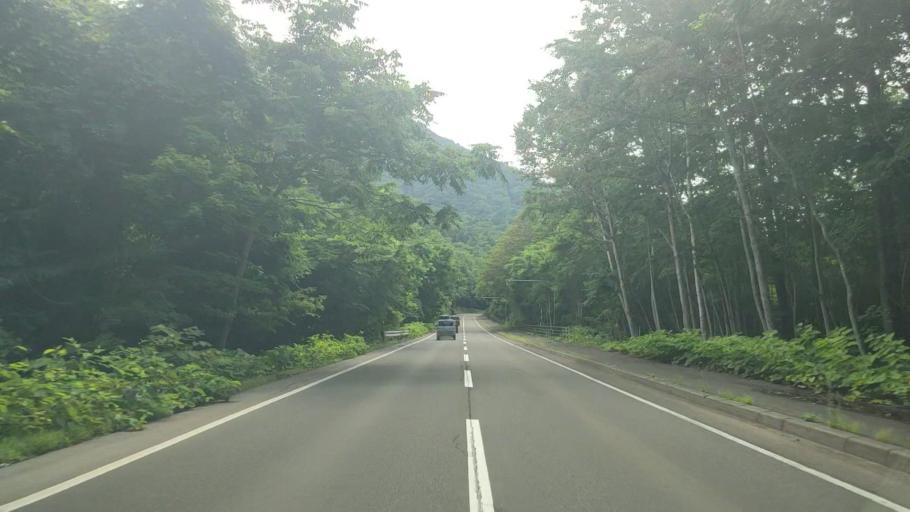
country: JP
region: Hokkaido
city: Shiraoi
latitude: 42.7366
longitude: 141.3787
